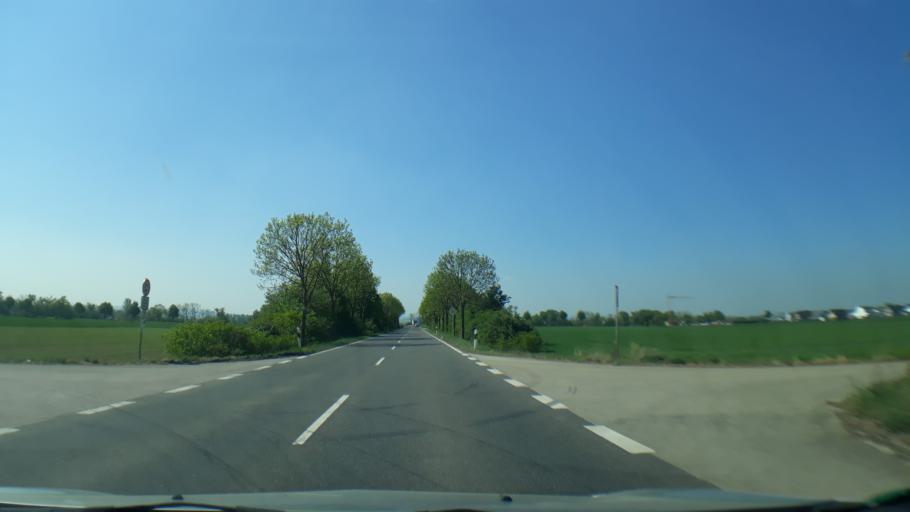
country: DE
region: North Rhine-Westphalia
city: Zulpich
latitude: 50.6877
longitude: 6.6692
